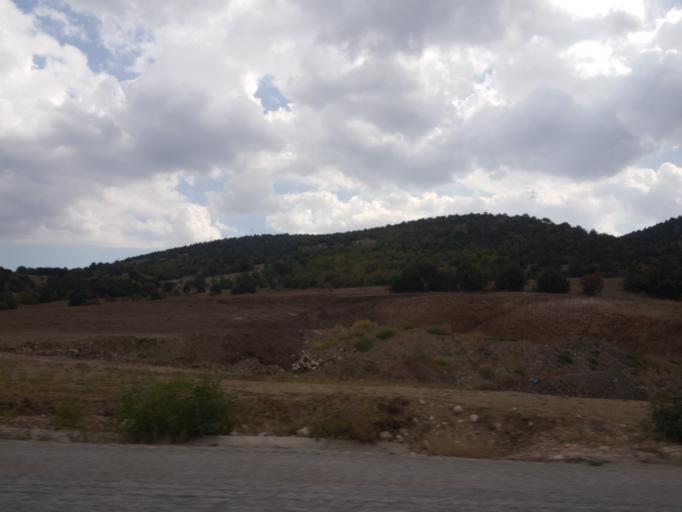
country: TR
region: Yozgat
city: Aydincik
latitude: 40.1873
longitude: 35.3987
